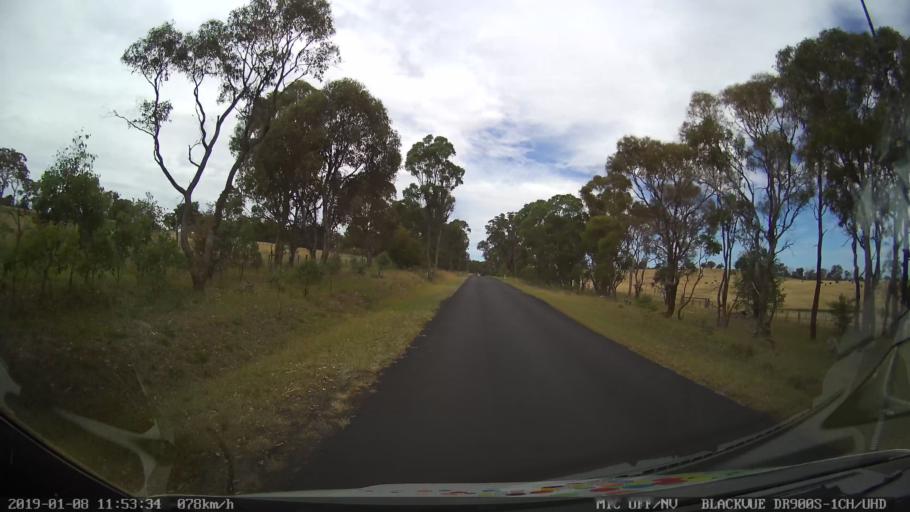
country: AU
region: New South Wales
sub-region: Armidale Dumaresq
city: Armidale
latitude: -30.4160
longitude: 151.5615
